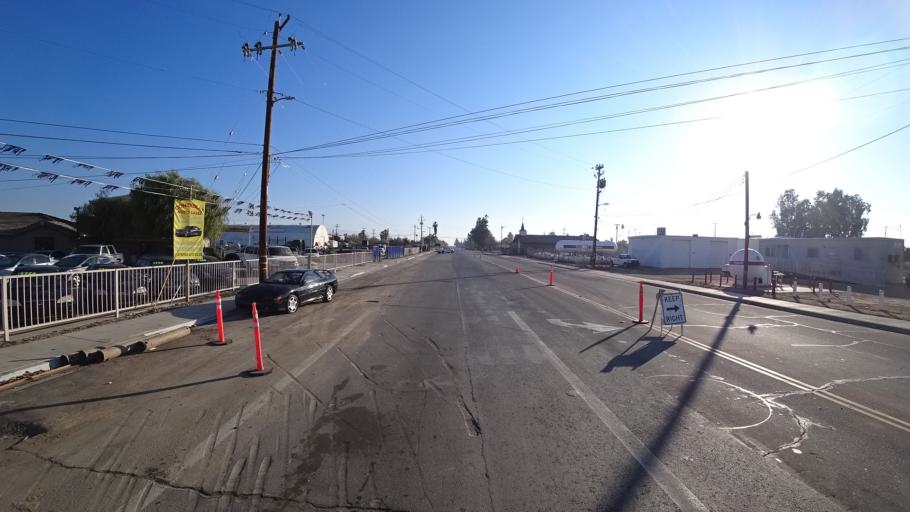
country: US
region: California
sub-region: Kern County
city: Greenfield
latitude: 35.3032
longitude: -119.0027
